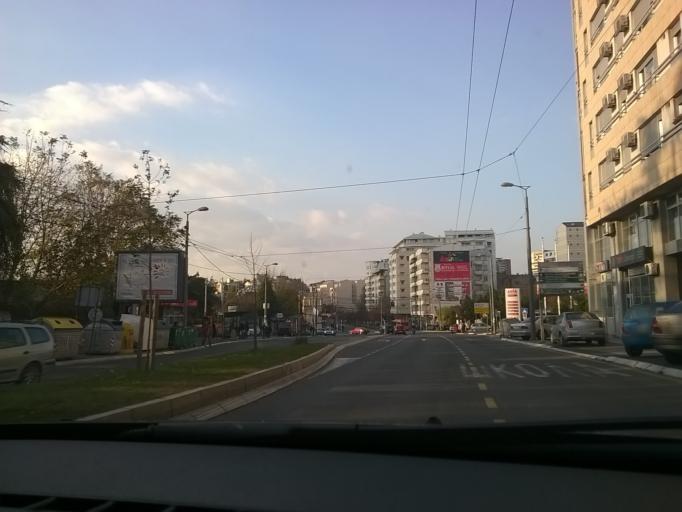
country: RS
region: Central Serbia
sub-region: Belgrade
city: Vracar
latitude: 44.7905
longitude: 20.4985
